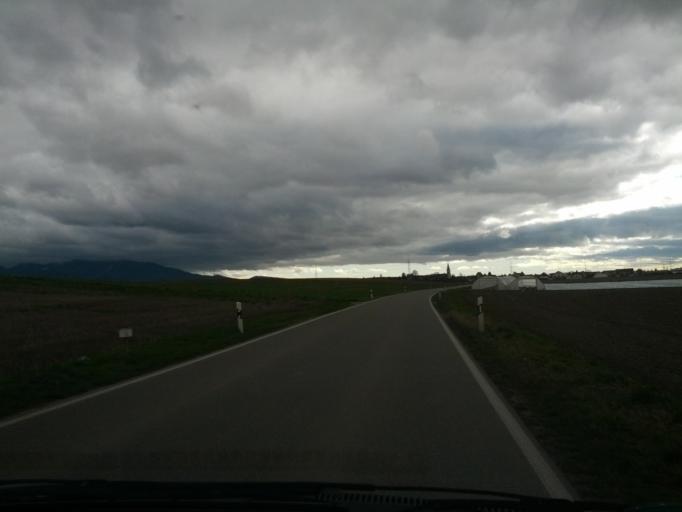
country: DE
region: Baden-Wuerttemberg
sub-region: Freiburg Region
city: Eschbach
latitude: 47.9012
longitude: 7.6594
